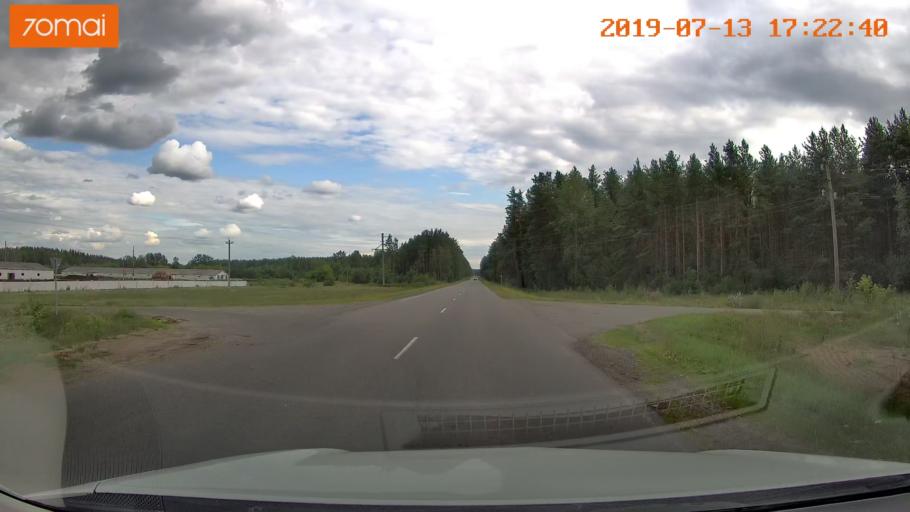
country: BY
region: Mogilev
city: Babruysk
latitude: 53.2688
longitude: 29.2349
